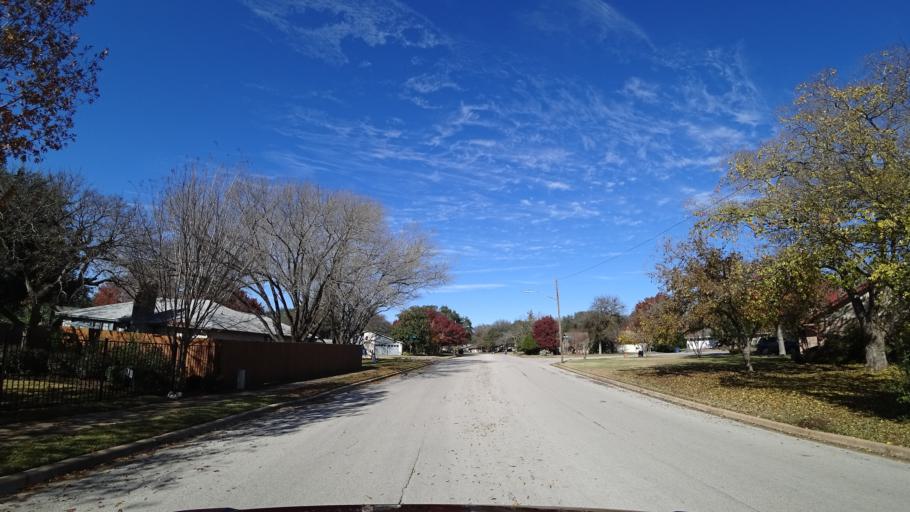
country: US
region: Texas
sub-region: Travis County
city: Wells Branch
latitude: 30.4278
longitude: -97.7092
